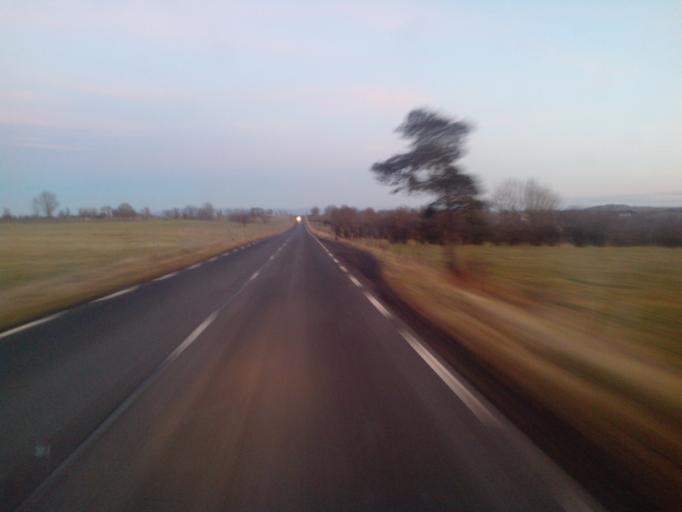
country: FR
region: Auvergne
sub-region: Departement du Cantal
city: Neussargues-Moissac
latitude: 45.0627
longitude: 2.9859
